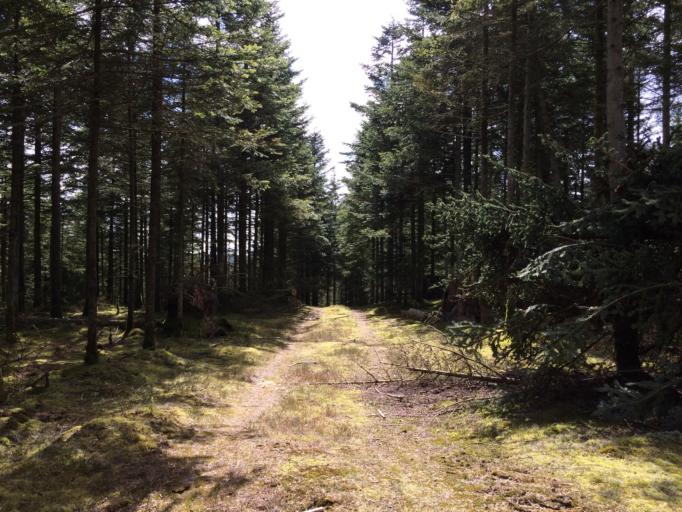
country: DK
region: Central Jutland
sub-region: Holstebro Kommune
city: Ulfborg
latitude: 56.2511
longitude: 8.4265
